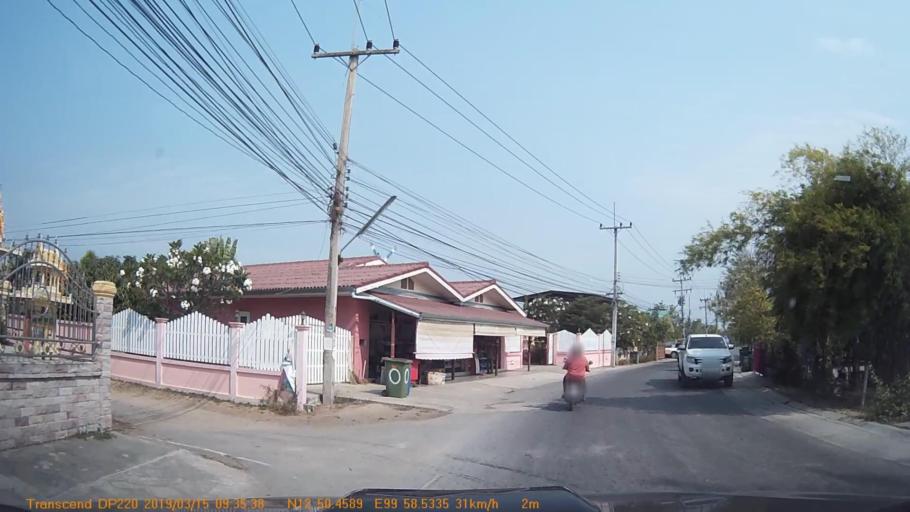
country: TH
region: Phetchaburi
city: Cha-am
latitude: 12.8412
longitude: 99.9755
